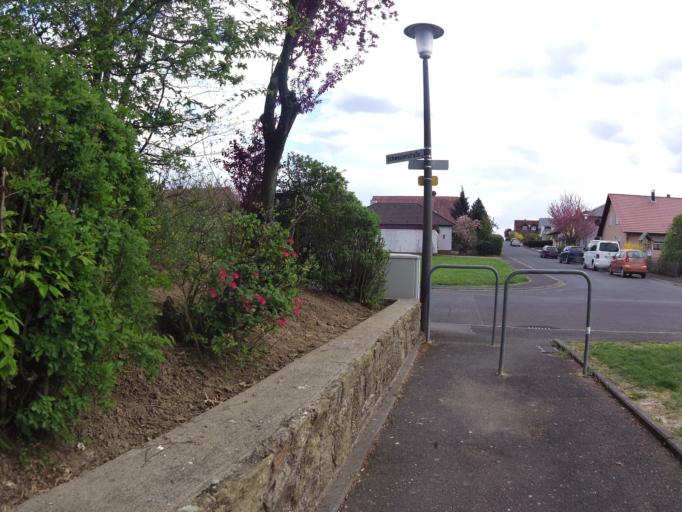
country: DE
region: Bavaria
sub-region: Regierungsbezirk Unterfranken
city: Oberpleichfeld
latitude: 49.8748
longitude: 10.0884
